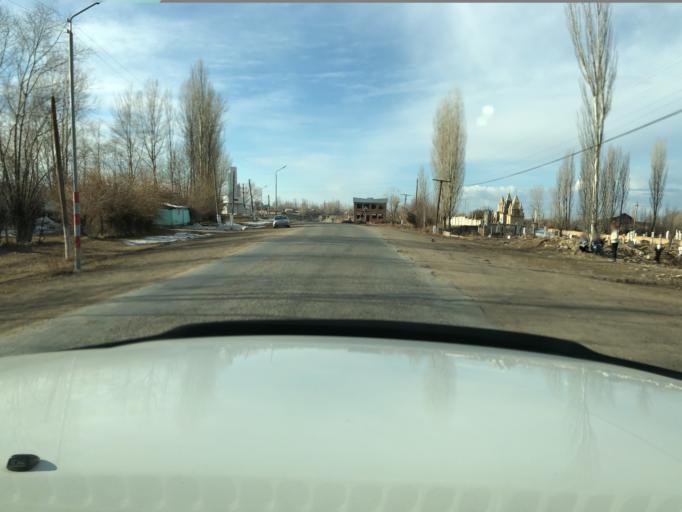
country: KG
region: Ysyk-Koel
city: Pokrovka
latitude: 42.3203
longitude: 77.9082
